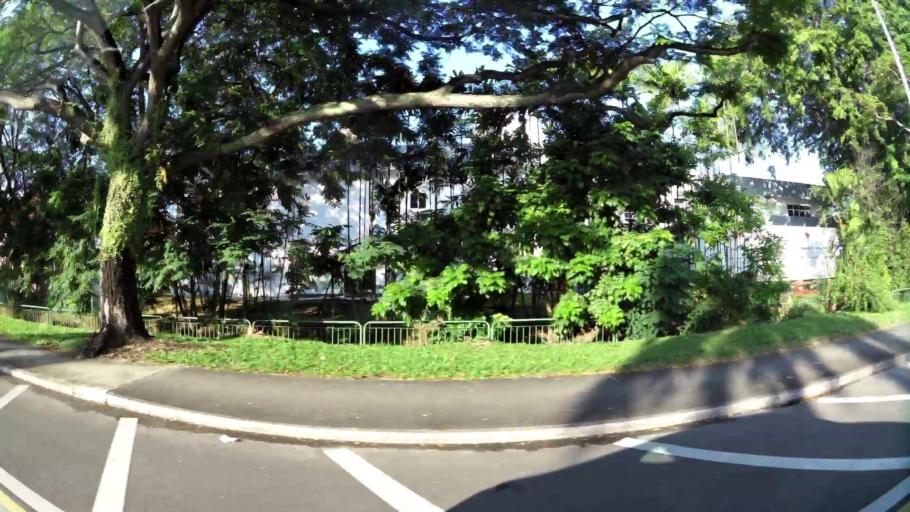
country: SG
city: Singapore
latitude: 1.3181
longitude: 103.9328
